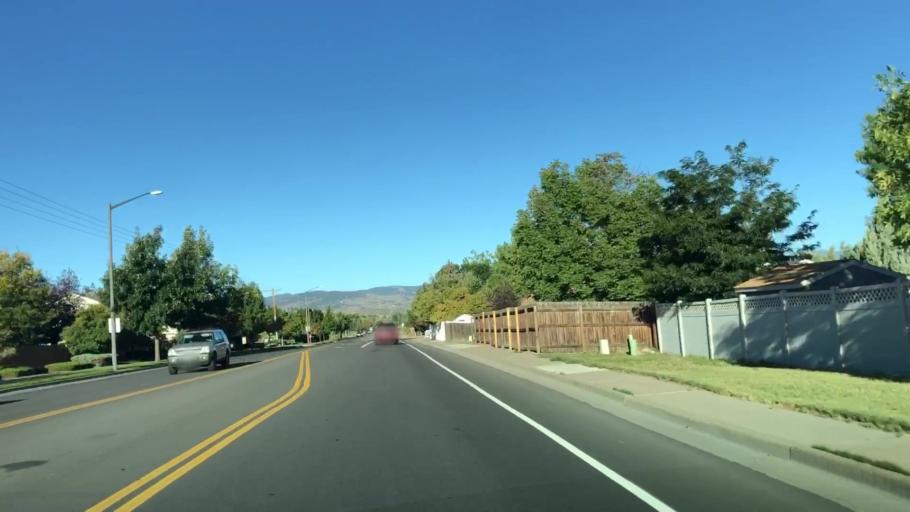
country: US
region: Colorado
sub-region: Larimer County
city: Loveland
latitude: 40.3785
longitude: -105.1177
